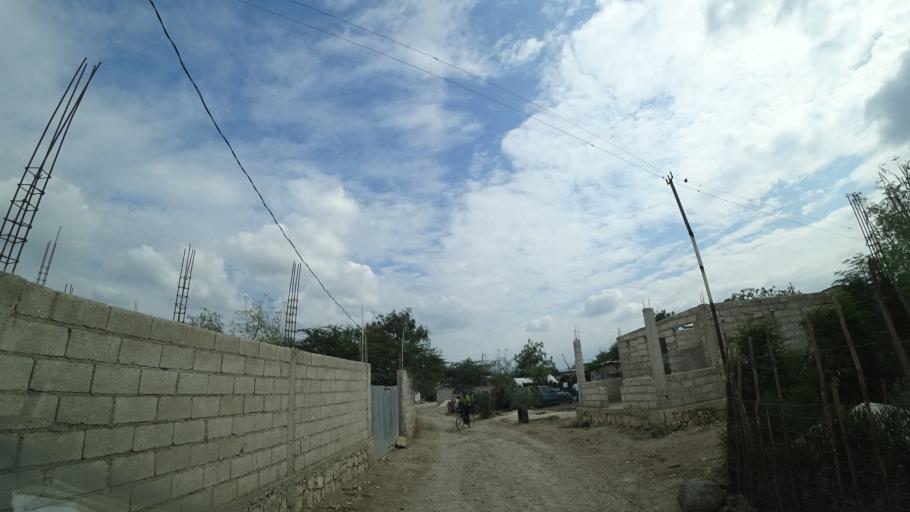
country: HT
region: Ouest
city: Croix des Bouquets
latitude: 18.6625
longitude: -72.2550
